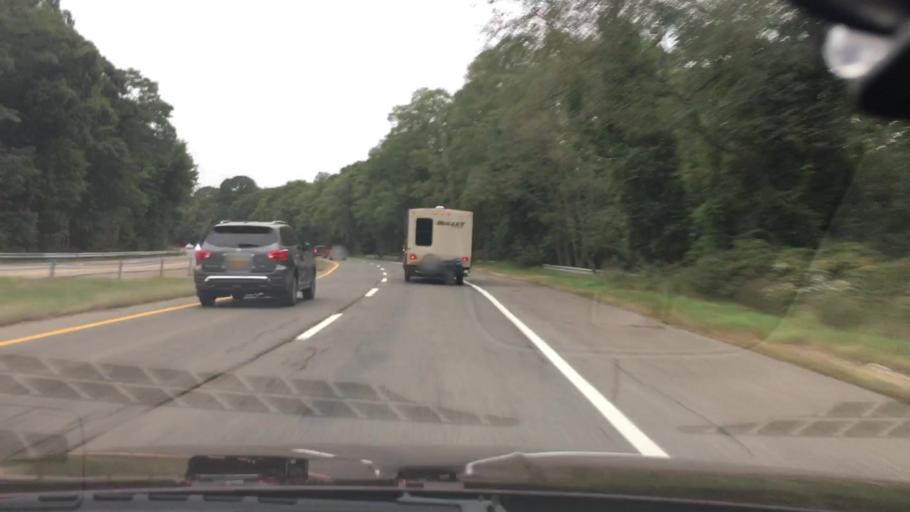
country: US
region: New York
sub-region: Suffolk County
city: Setauket-East Setauket
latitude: 40.9113
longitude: -73.1181
